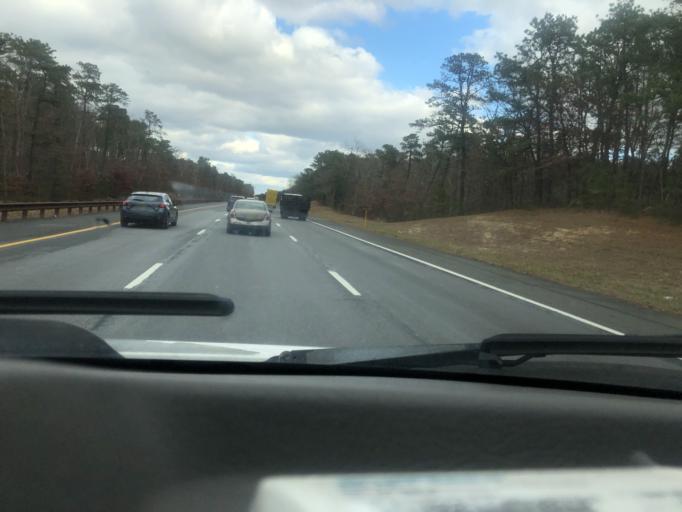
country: US
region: New Jersey
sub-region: Ocean County
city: Manahawkin
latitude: 39.6960
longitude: -74.2937
